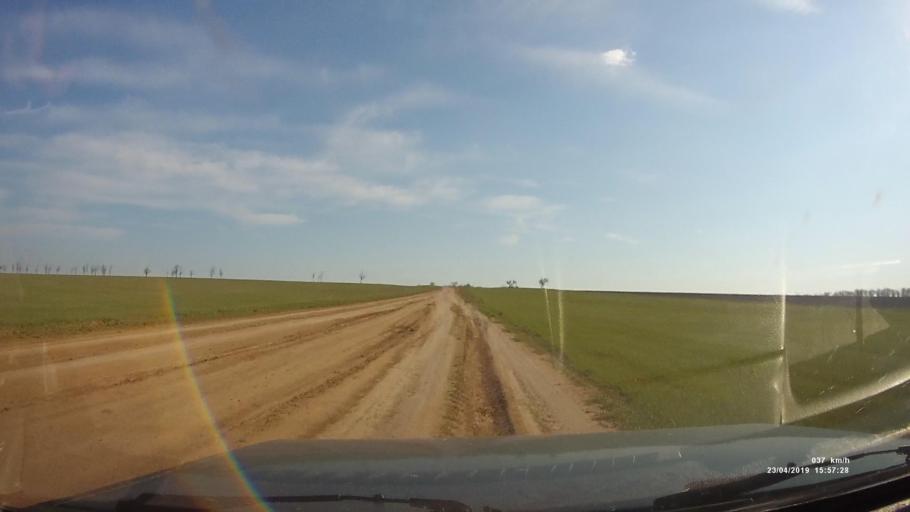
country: RU
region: Rostov
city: Remontnoye
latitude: 46.5316
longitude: 43.1099
